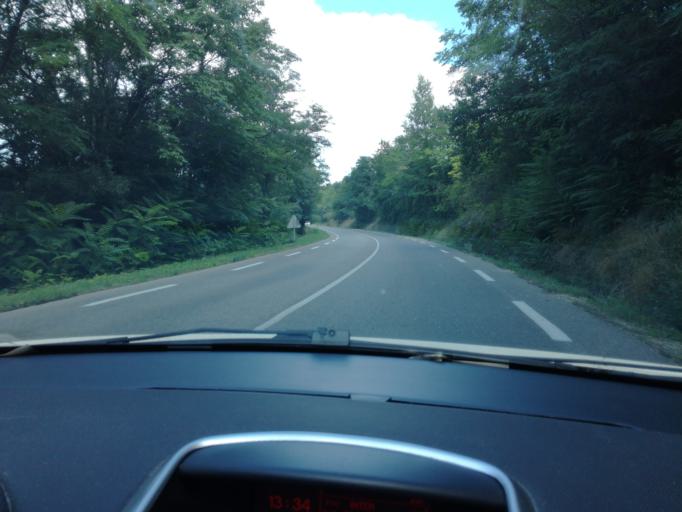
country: FR
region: Rhone-Alpes
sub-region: Departement de l'Ardeche
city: Ruoms
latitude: 44.4879
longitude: 4.3812
